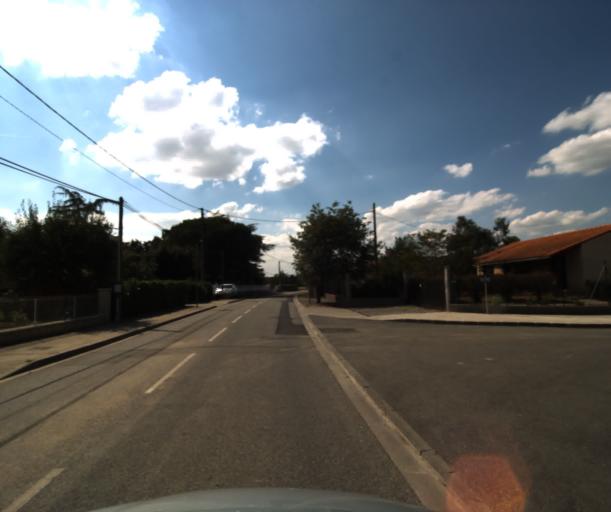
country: FR
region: Midi-Pyrenees
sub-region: Departement de la Haute-Garonne
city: Saint-Lys
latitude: 43.5166
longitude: 1.1711
